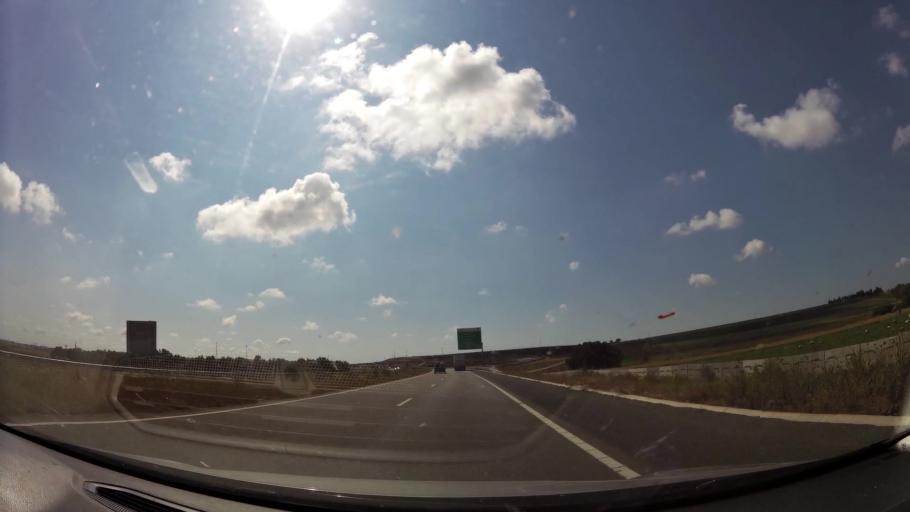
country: MA
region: Rabat-Sale-Zemmour-Zaer
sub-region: Skhirate-Temara
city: Temara
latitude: 33.8455
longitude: -6.8936
